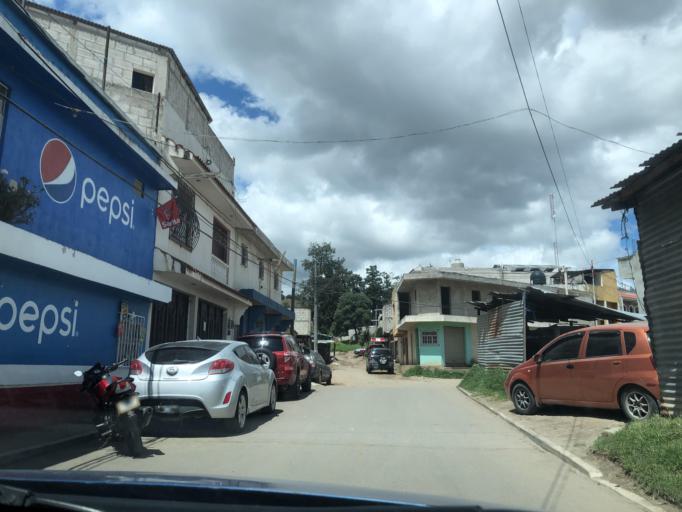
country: GT
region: Quetzaltenango
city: Quetzaltenango
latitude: 14.8383
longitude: -91.5459
